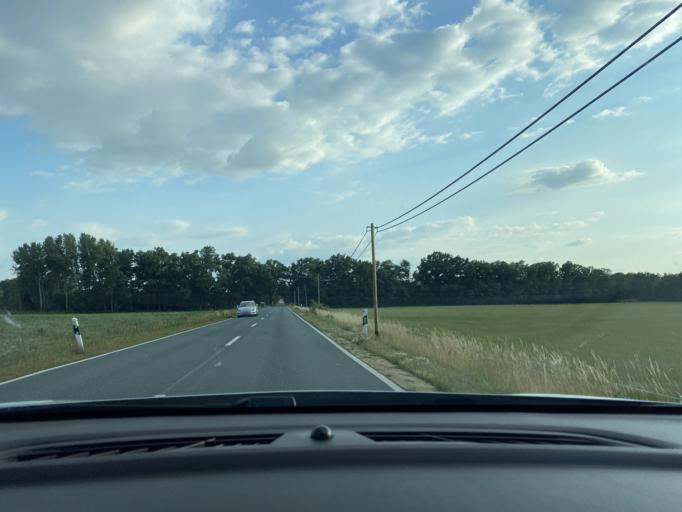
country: DE
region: Saxony
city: Konigswartha
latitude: 51.3261
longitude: 14.3399
